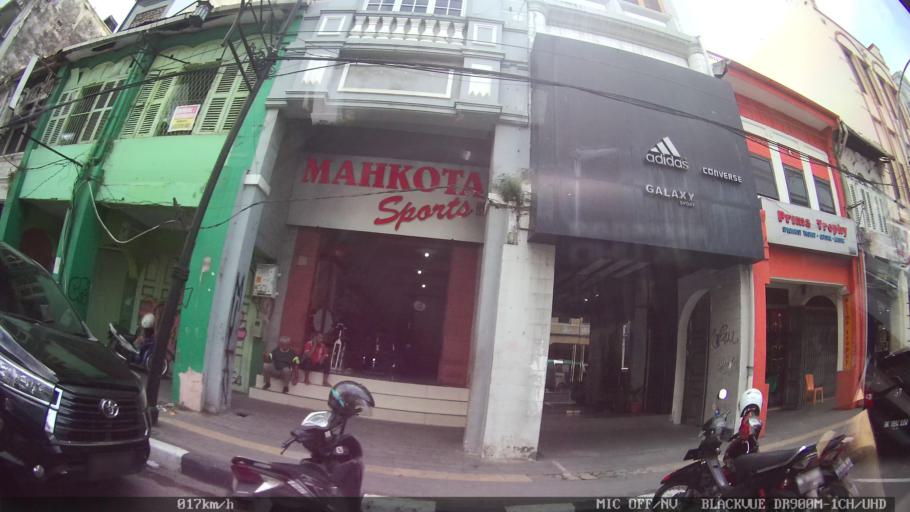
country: ID
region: North Sumatra
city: Medan
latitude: 3.5872
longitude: 98.6791
